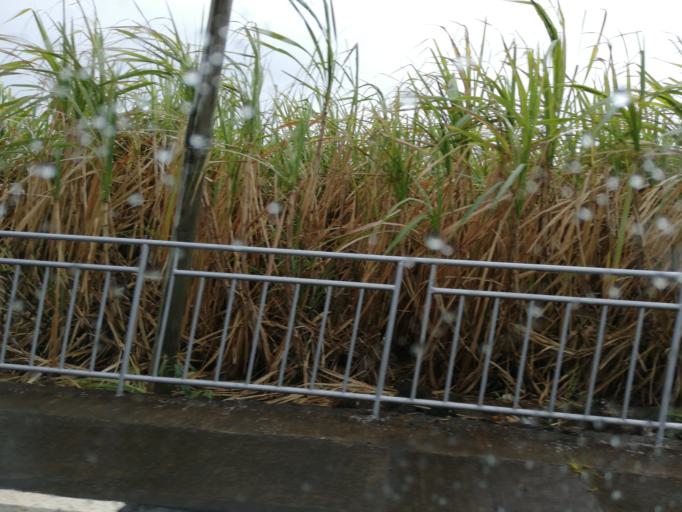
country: MU
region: Pamplemousses
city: Long Mountain
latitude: -20.1256
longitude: 57.5735
